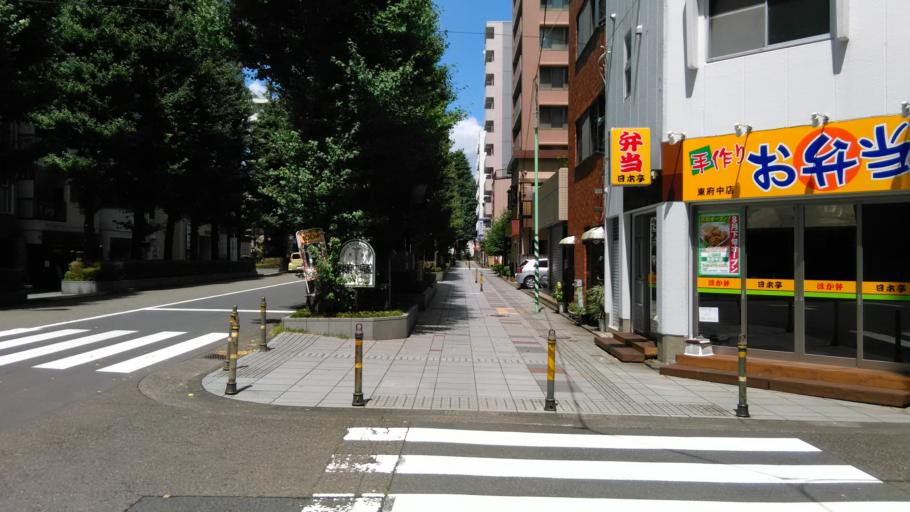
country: JP
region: Tokyo
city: Kokubunji
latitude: 35.6714
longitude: 139.4944
